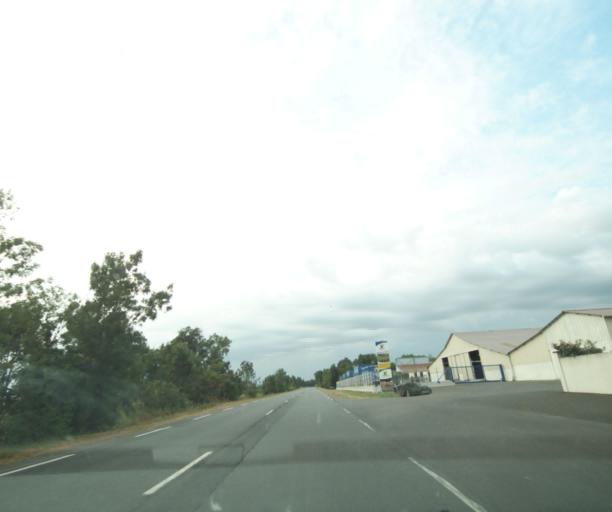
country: FR
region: Poitou-Charentes
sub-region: Departement de la Charente-Maritime
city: Marans
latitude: 46.3353
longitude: -0.9973
